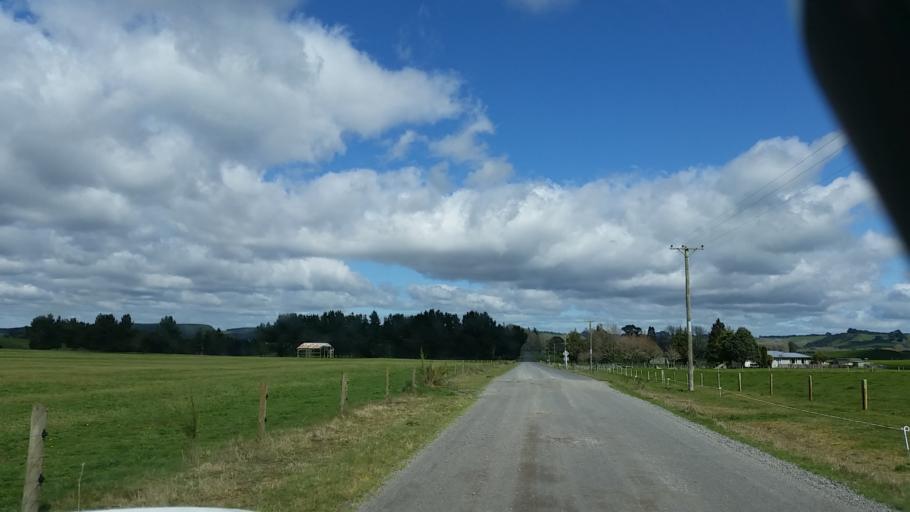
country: NZ
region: Bay of Plenty
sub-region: Whakatane District
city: Murupara
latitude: -38.3119
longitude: 176.5560
